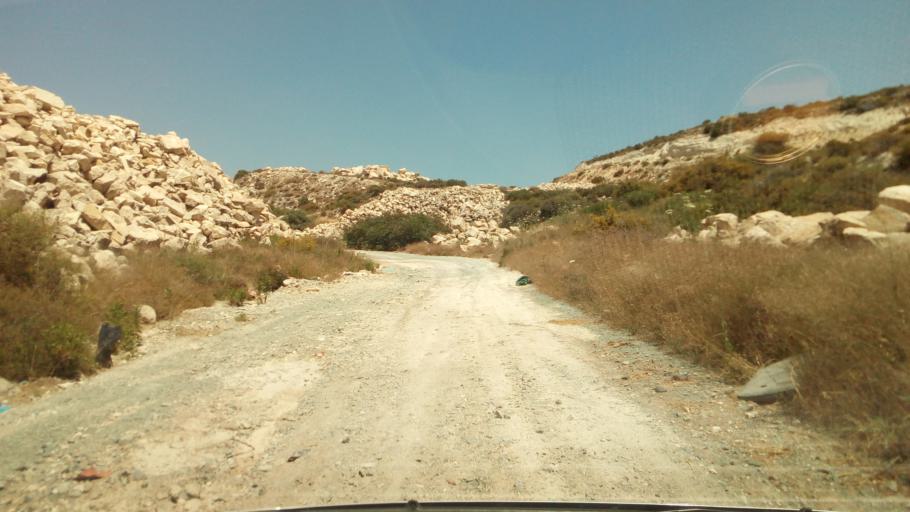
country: CY
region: Limassol
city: Ypsonas
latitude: 34.7227
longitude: 32.9567
